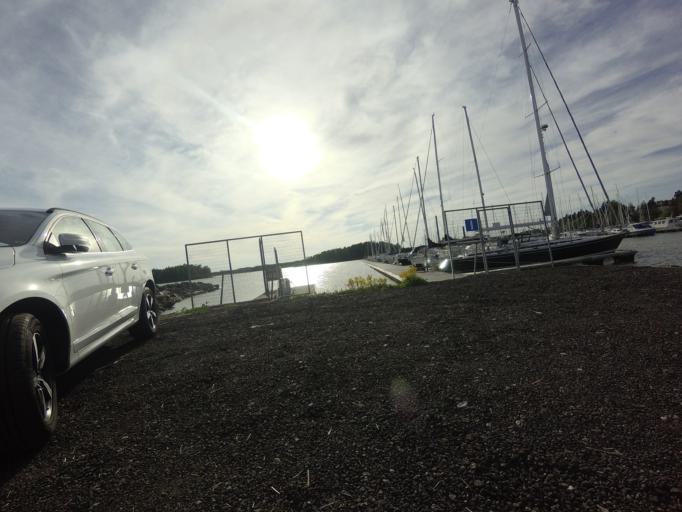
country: FI
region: Uusimaa
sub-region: Helsinki
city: Koukkuniemi
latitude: 60.1420
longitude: 24.7377
